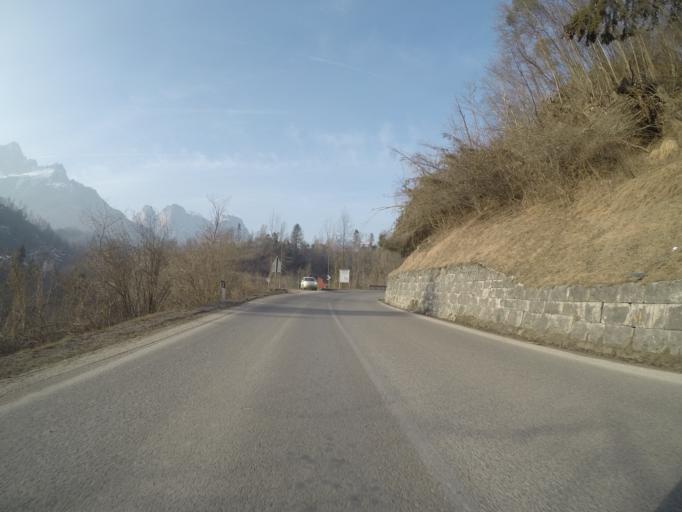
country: IT
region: Veneto
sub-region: Provincia di Belluno
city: Agordo
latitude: 46.2689
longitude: 12.0395
